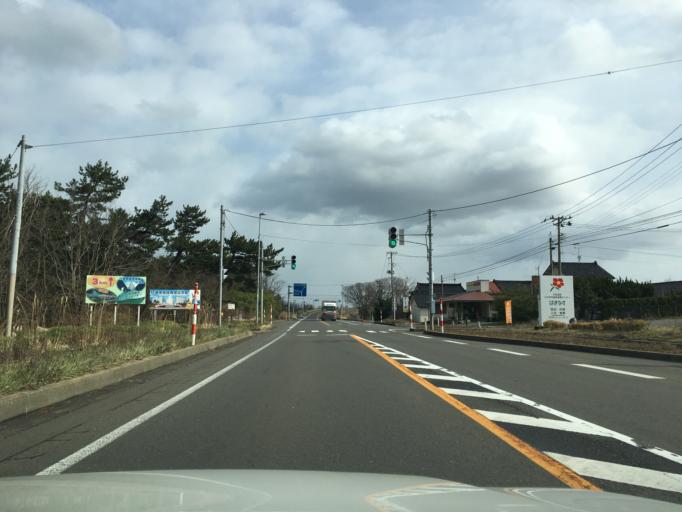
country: JP
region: Yamagata
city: Yuza
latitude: 39.2390
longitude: 139.9121
